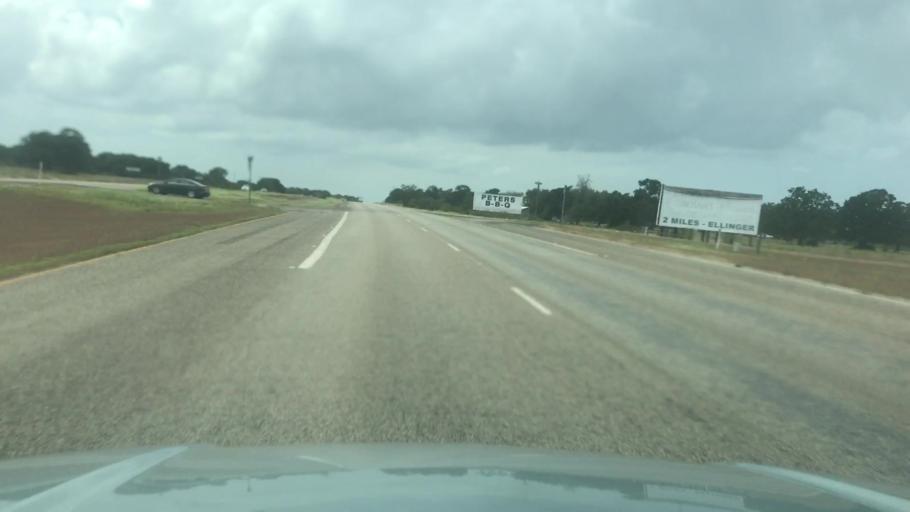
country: US
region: Texas
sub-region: Colorado County
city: Weimar
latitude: 29.8161
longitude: -96.6837
